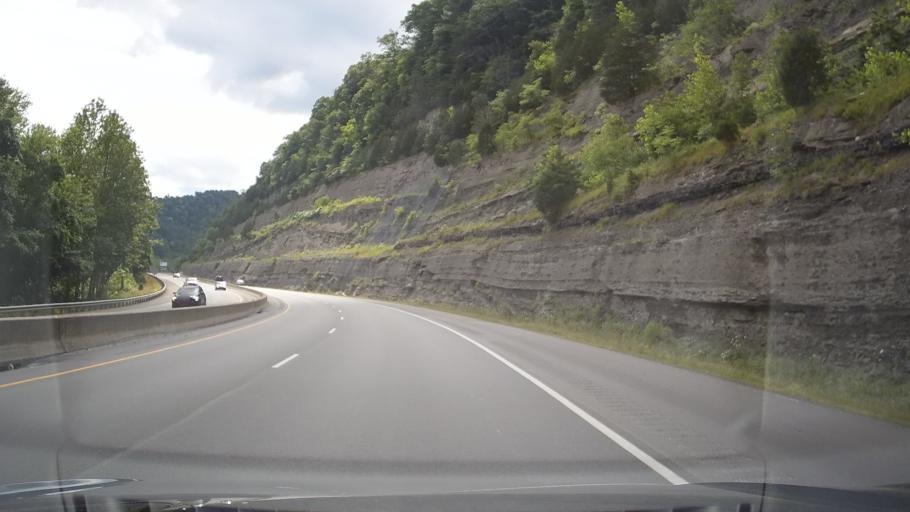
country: US
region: Kentucky
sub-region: Floyd County
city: Prestonsburg
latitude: 37.5946
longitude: -82.6666
